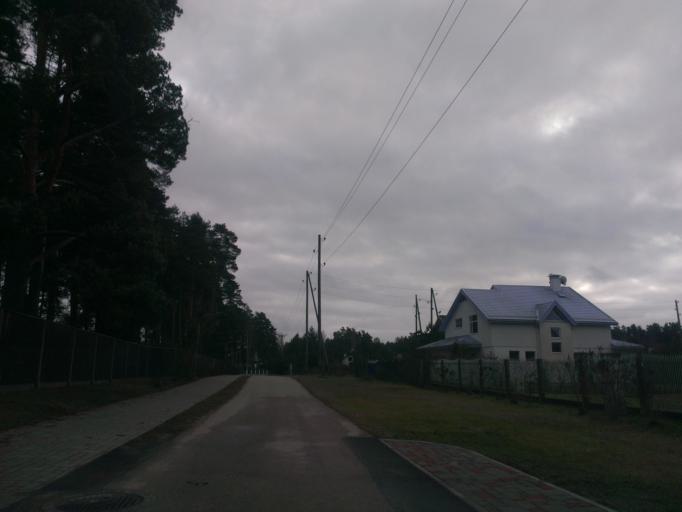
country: LV
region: Riga
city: Bergi
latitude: 56.9898
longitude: 24.3064
